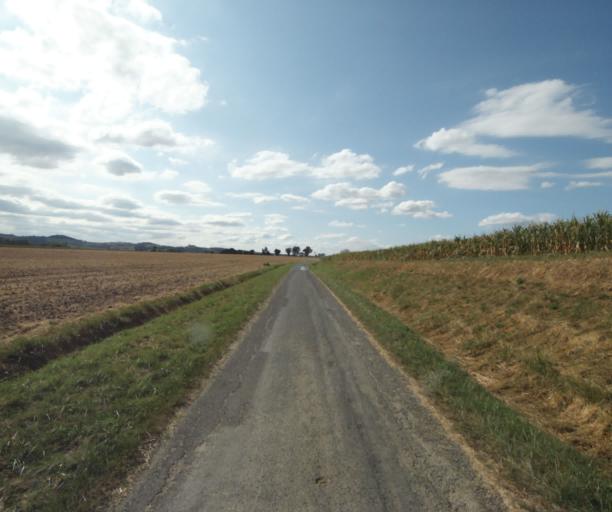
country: FR
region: Midi-Pyrenees
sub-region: Departement du Tarn
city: Puylaurens
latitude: 43.5215
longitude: 1.9817
